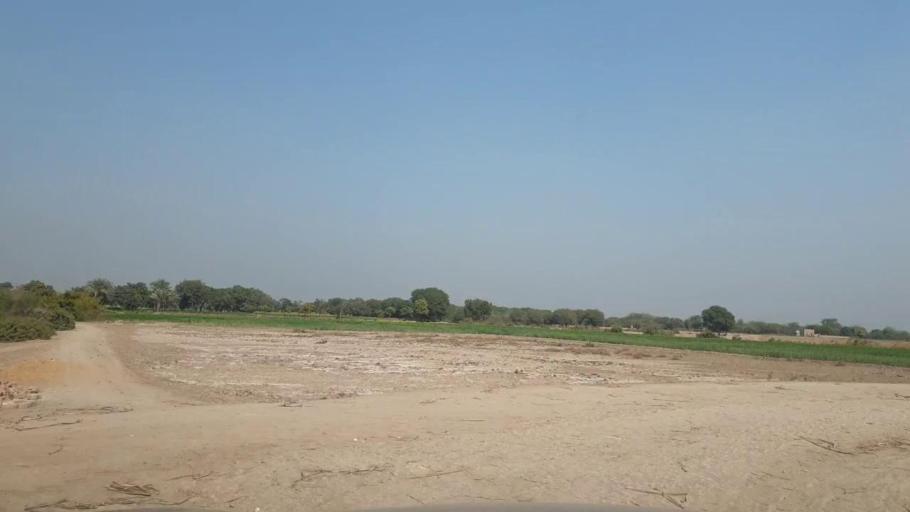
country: PK
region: Sindh
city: Tando Allahyar
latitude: 25.5499
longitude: 68.7142
